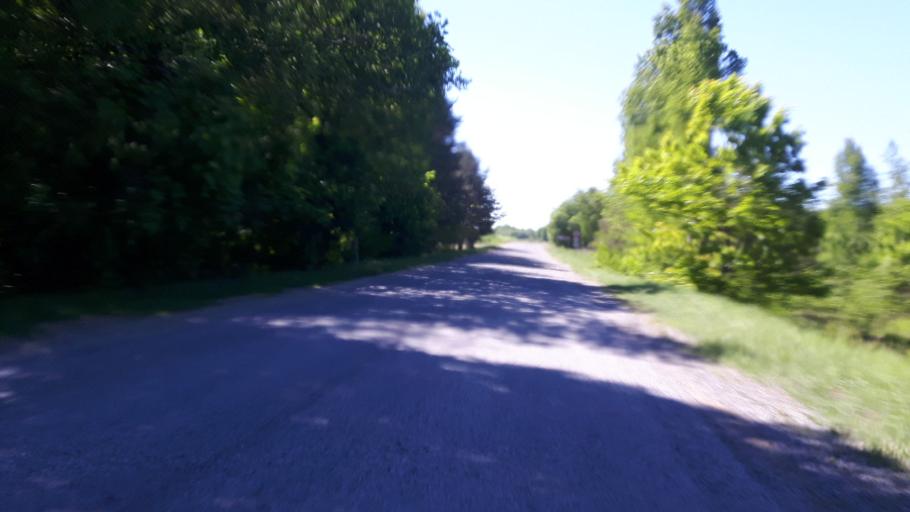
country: EE
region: Ida-Virumaa
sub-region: Sillamaee linn
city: Sillamae
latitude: 59.3754
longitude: 27.8545
